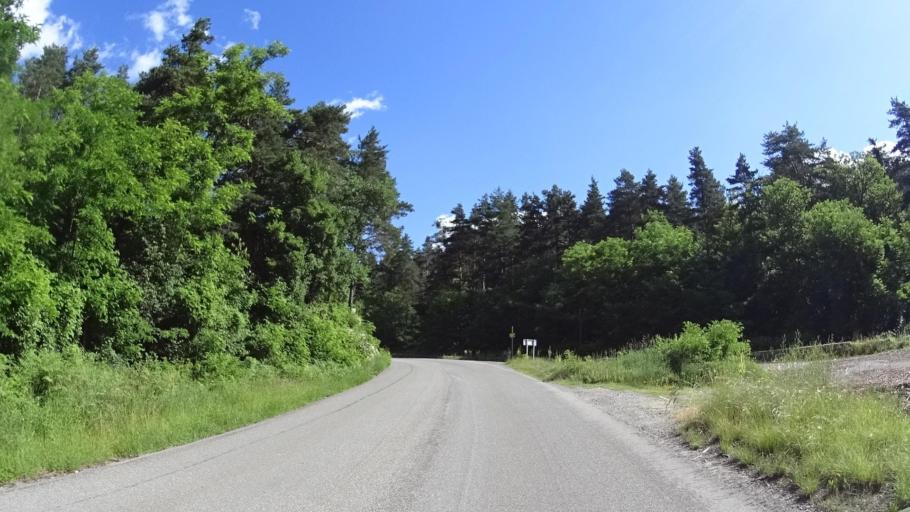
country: FR
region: Provence-Alpes-Cote d'Azur
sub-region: Departement des Alpes-de-Haute-Provence
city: Annot
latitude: 43.9816
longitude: 6.6499
